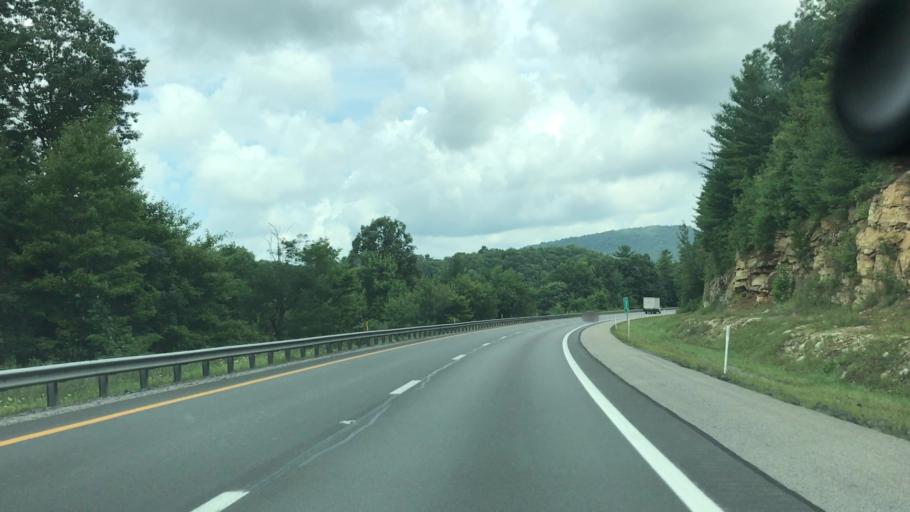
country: US
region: West Virginia
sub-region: Raleigh County
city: Shady Spring
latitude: 37.6642
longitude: -81.1154
